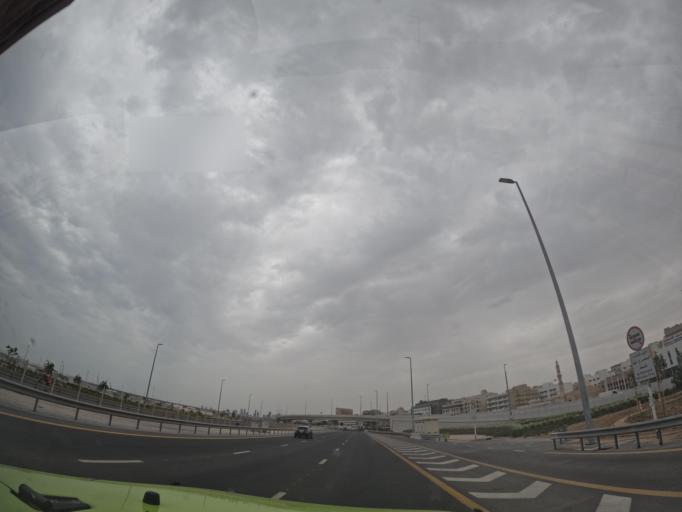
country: AE
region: Ash Shariqah
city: Sharjah
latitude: 25.2815
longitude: 55.3117
